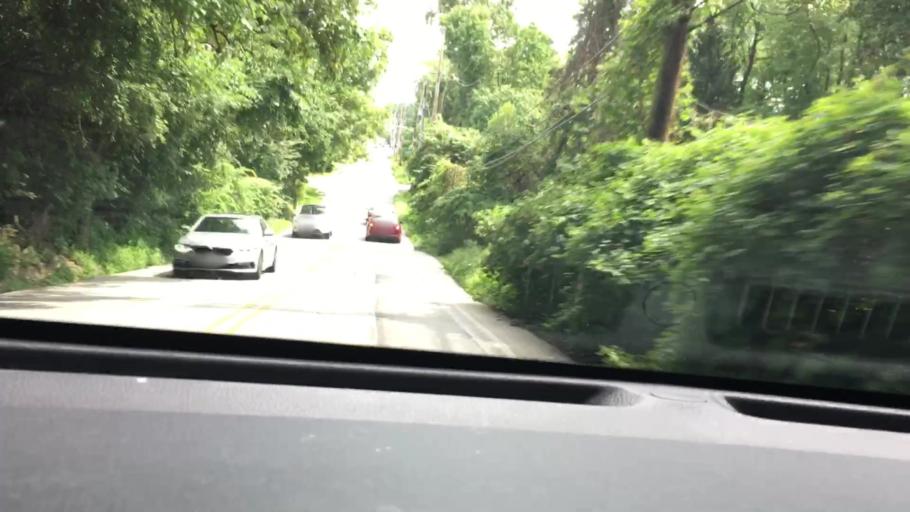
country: US
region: Pennsylvania
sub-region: Bucks County
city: Feasterville
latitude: 40.1311
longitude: -75.0280
